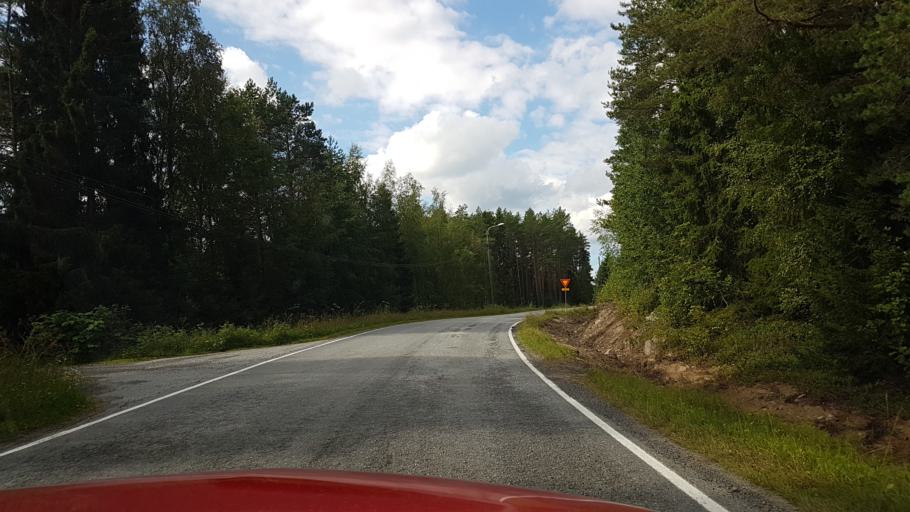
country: FI
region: Northern Ostrobothnia
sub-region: Ylivieska
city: Himanka
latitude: 64.0645
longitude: 23.6715
